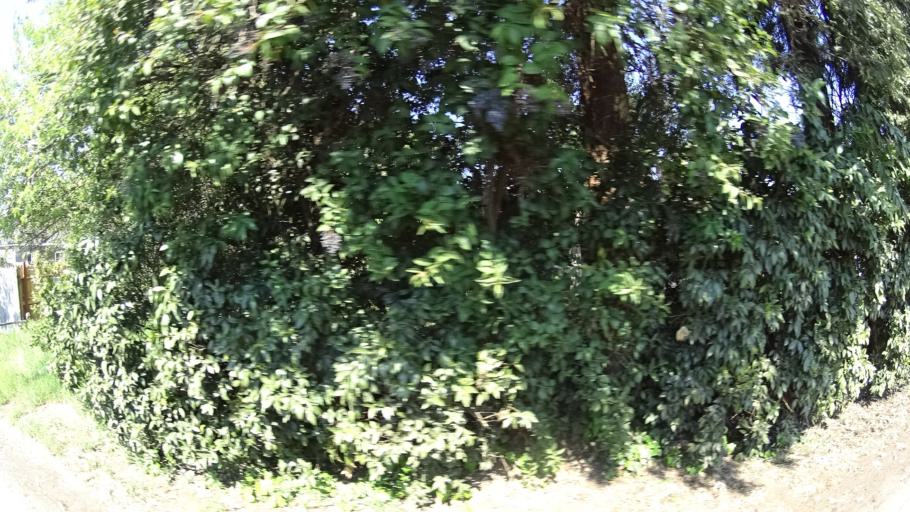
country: US
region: California
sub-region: Fresno County
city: Fresno
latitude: 36.7939
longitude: -119.8077
